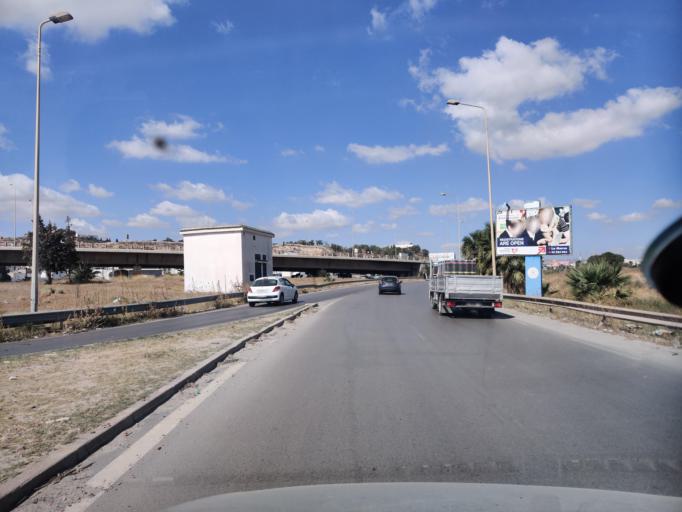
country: TN
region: Bin 'Arus
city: Ben Arous
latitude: 36.7816
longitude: 10.1985
